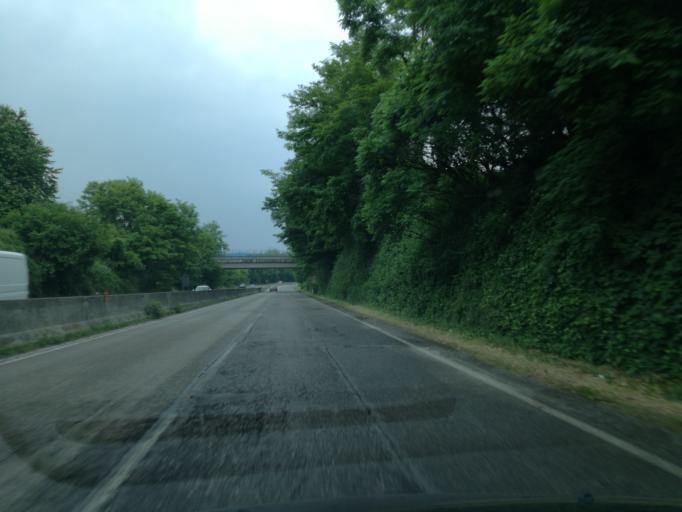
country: IT
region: Lombardy
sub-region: Provincia di Monza e Brianza
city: Villasanta
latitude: 45.6008
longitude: 9.3180
